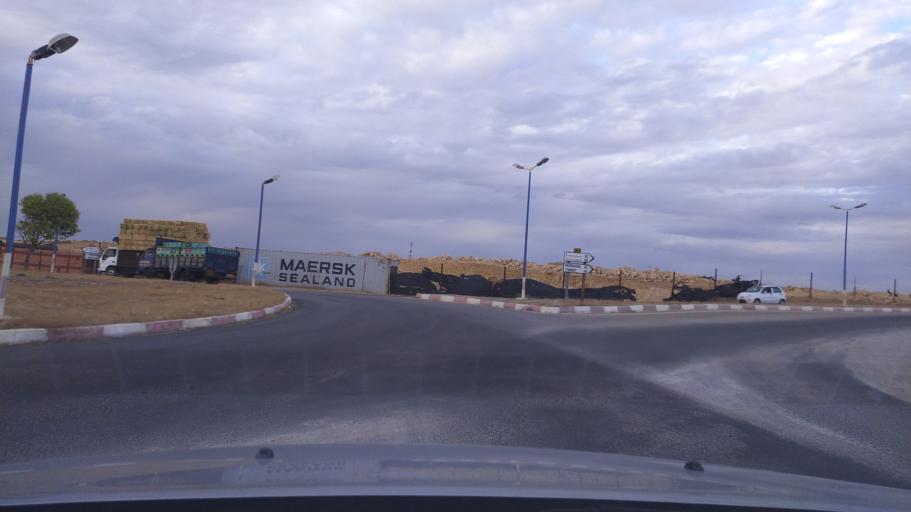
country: DZ
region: Tiaret
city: Frenda
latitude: 34.9919
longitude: 1.1302
